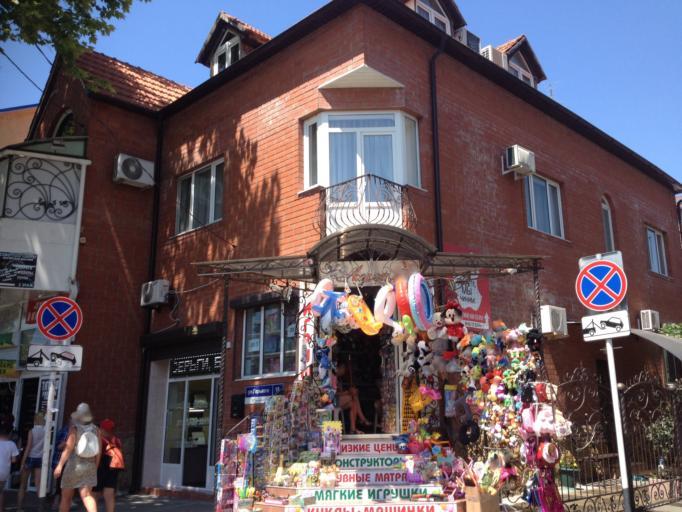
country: RU
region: Krasnodarskiy
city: Anapa
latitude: 44.8983
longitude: 37.3213
